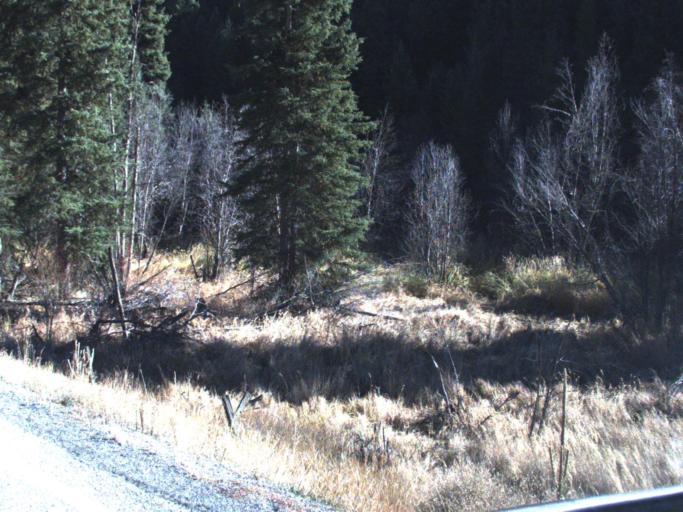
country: US
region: Washington
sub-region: Ferry County
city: Republic
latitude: 48.6056
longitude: -118.5991
